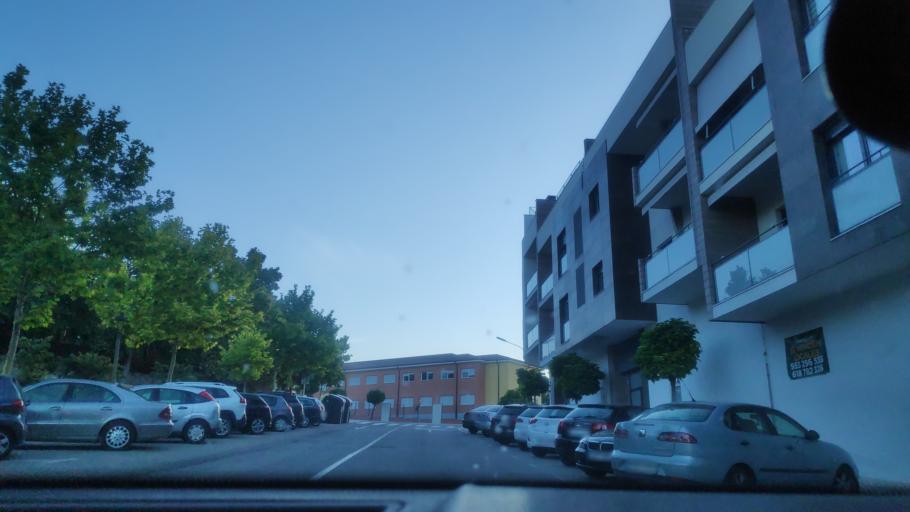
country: ES
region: Andalusia
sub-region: Provincia de Jaen
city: Jaen
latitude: 37.7827
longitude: -3.8141
